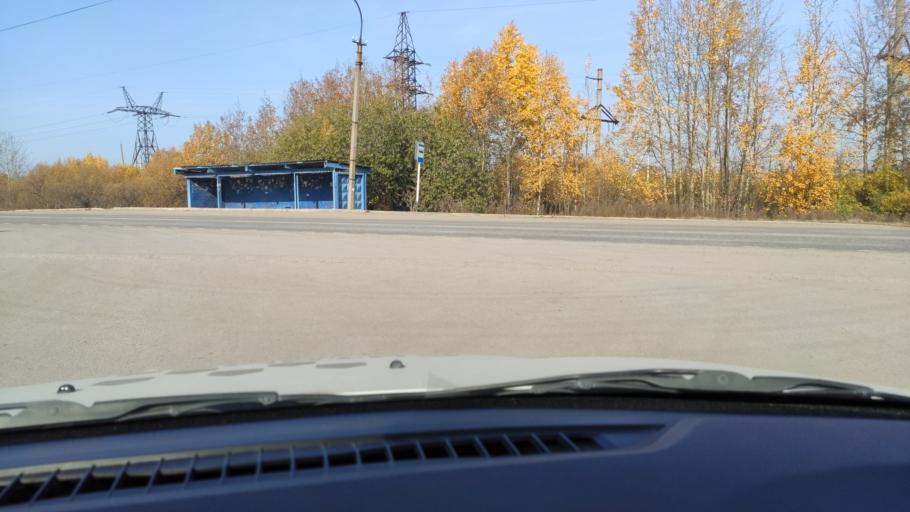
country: RU
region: Perm
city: Sylva
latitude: 58.0265
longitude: 56.7334
